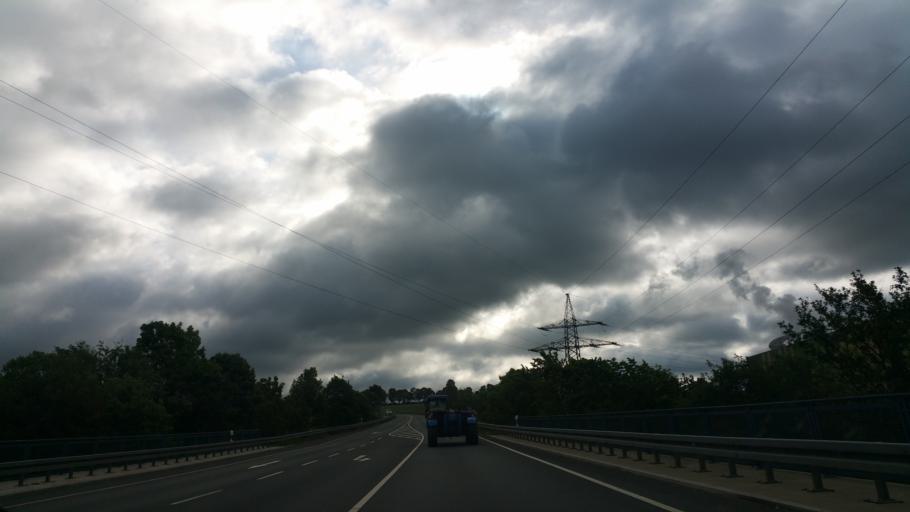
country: DE
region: Bavaria
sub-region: Upper Franconia
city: Schwarzenbach an der Saale
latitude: 50.2268
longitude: 11.9560
